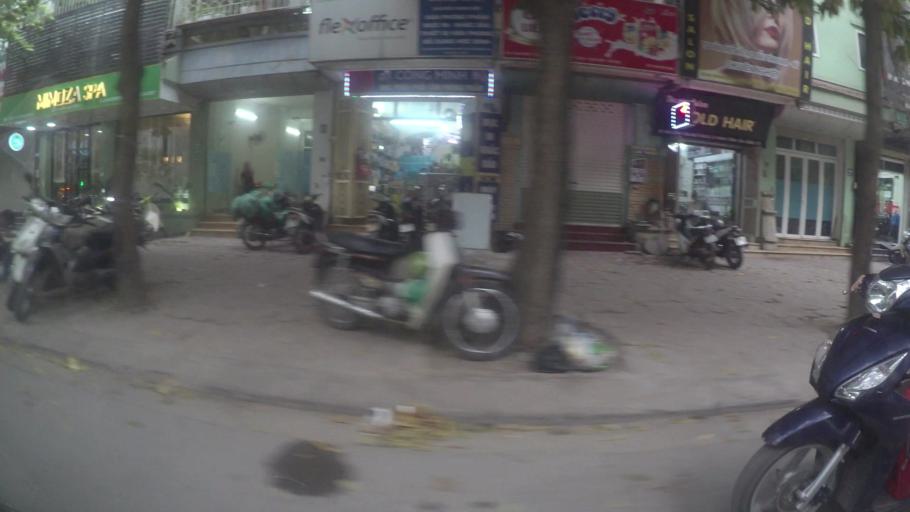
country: VN
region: Ha Noi
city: Cau Dien
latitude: 21.0350
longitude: 105.7730
